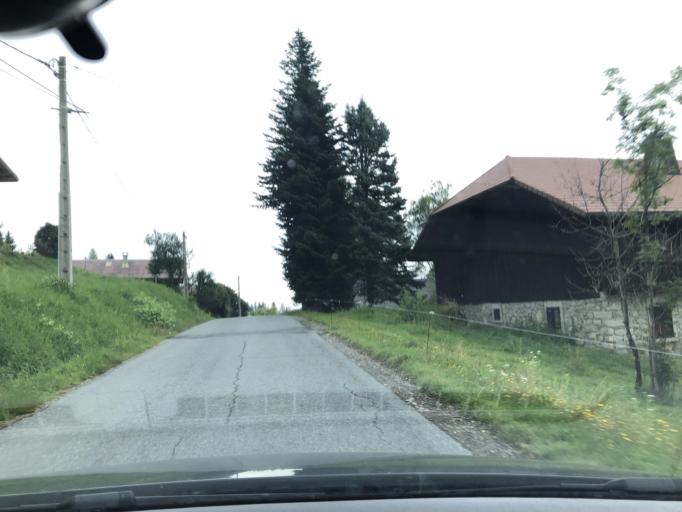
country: FR
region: Rhone-Alpes
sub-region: Departement de la Haute-Savoie
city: Combloux
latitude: 45.8976
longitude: 6.6189
